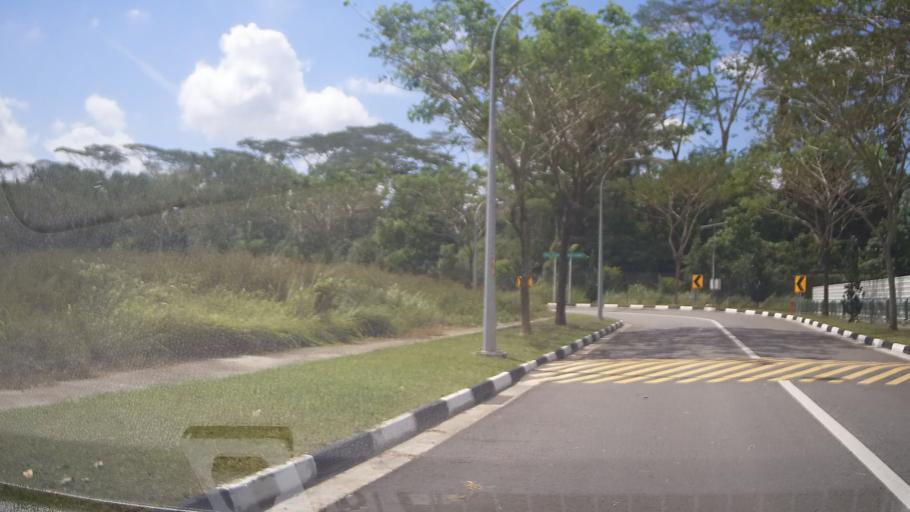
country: MY
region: Johor
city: Johor Bahru
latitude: 1.4192
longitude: 103.7220
